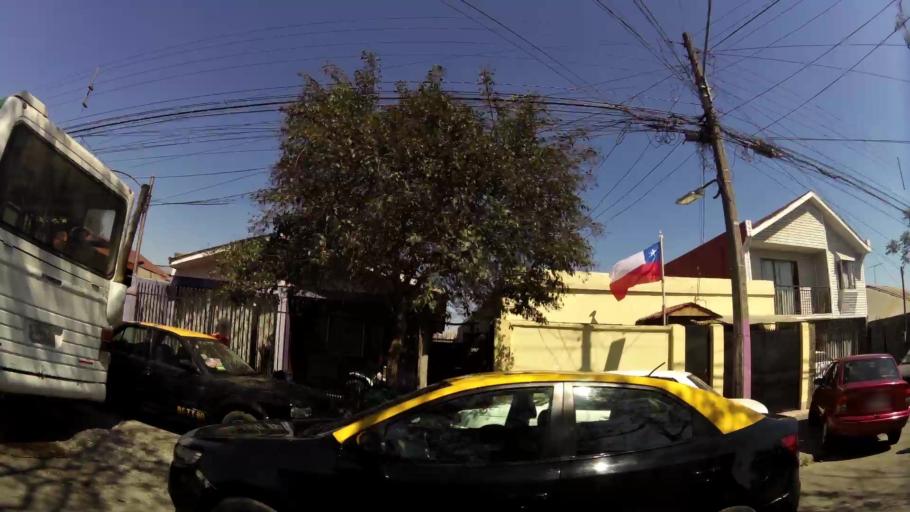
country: CL
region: Santiago Metropolitan
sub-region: Provincia de Santiago
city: La Pintana
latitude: -33.5302
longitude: -70.6497
